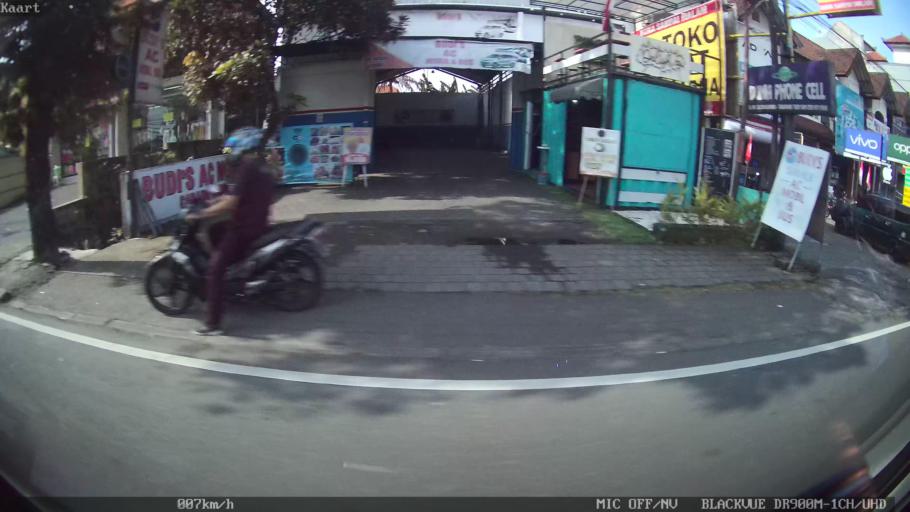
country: ID
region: Bali
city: Banjar Bongangede
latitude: -8.5500
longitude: 115.1238
